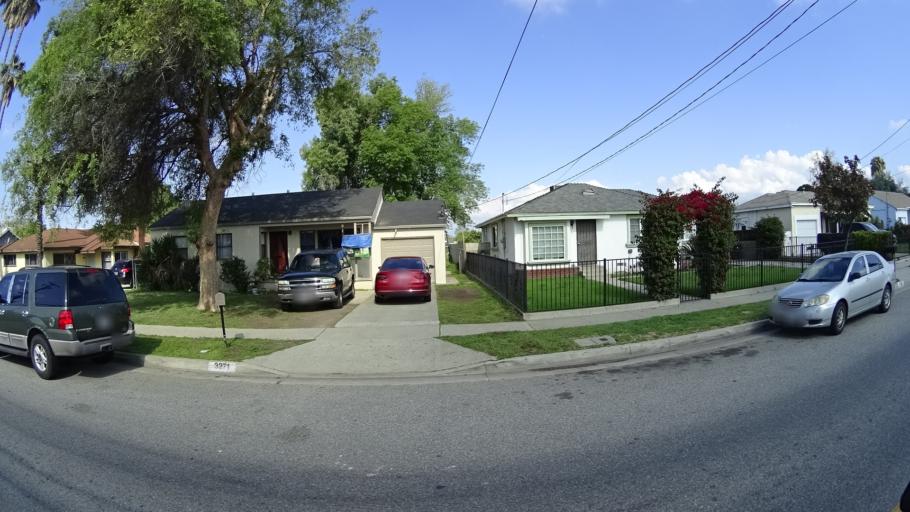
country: US
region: California
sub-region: Los Angeles County
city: Baldwin Park
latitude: 34.0736
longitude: -117.9669
